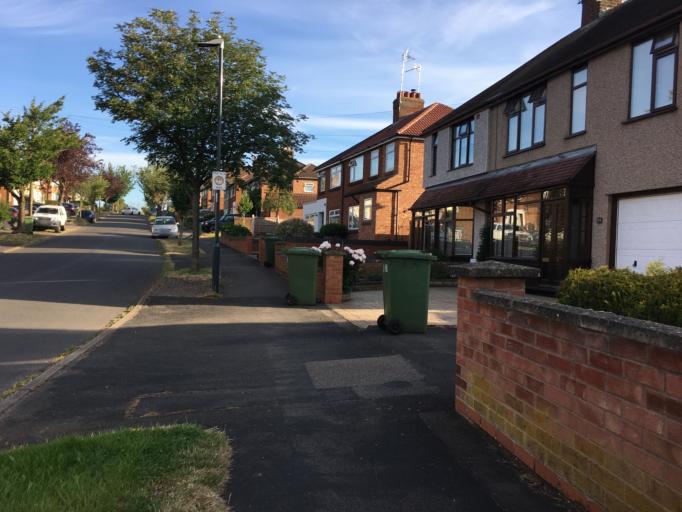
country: GB
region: England
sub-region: Warwickshire
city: Rugby
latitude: 52.3641
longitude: -1.2305
